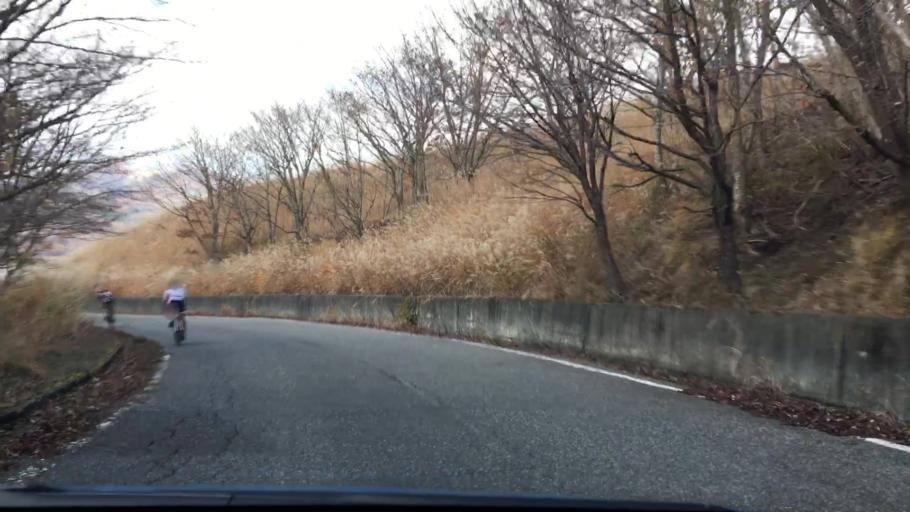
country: JP
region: Shizuoka
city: Gotemba
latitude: 35.4112
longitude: 138.9105
